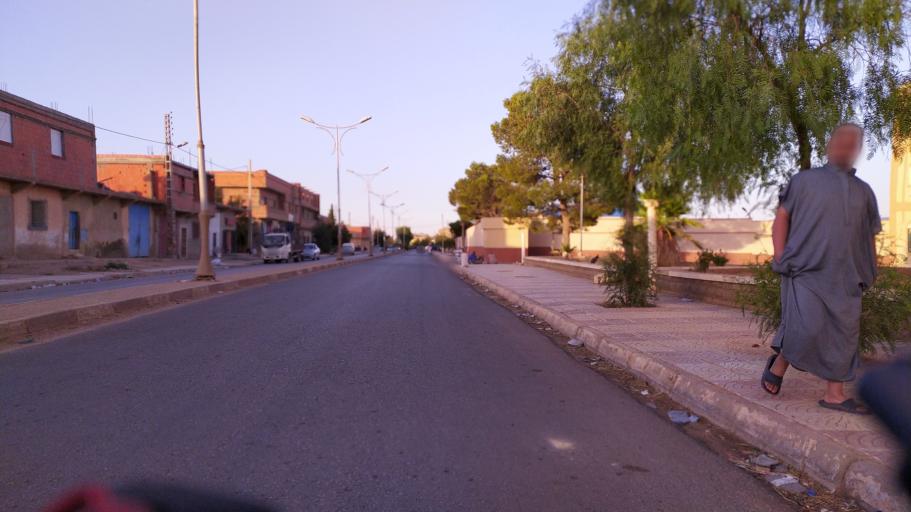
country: DZ
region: Tiaret
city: Frenda
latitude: 34.8896
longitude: 1.2432
